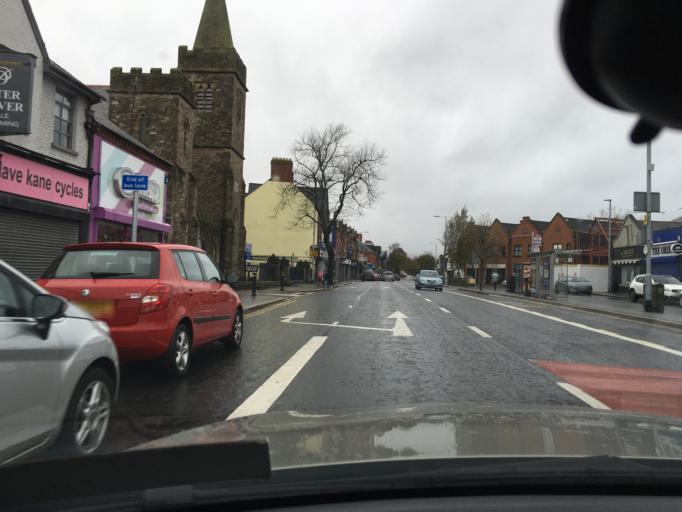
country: GB
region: Northern Ireland
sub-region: Castlereagh District
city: Castlereagh
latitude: 54.5950
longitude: -5.8664
